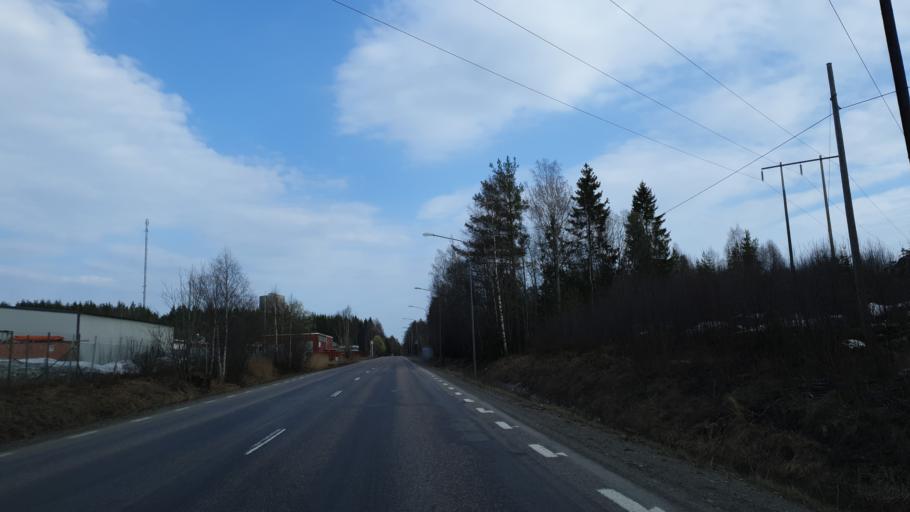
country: SE
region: Gaevleborg
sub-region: Hudiksvalls Kommun
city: Iggesund
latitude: 61.6453
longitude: 17.0532
